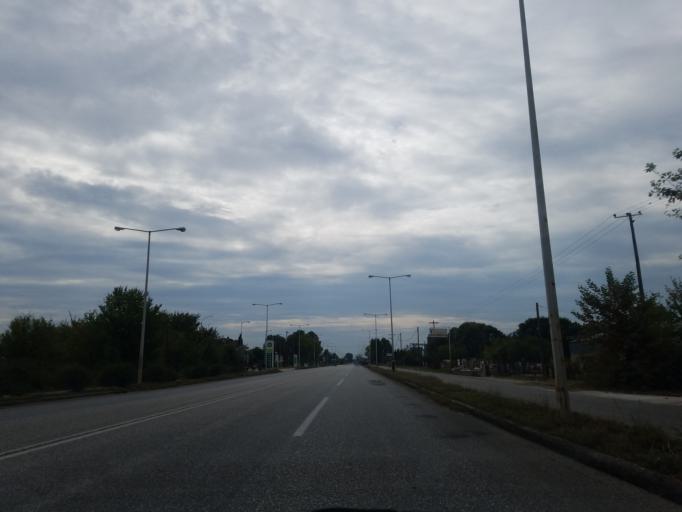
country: GR
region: Thessaly
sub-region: Trikala
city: Pyrgetos
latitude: 39.5790
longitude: 21.7428
